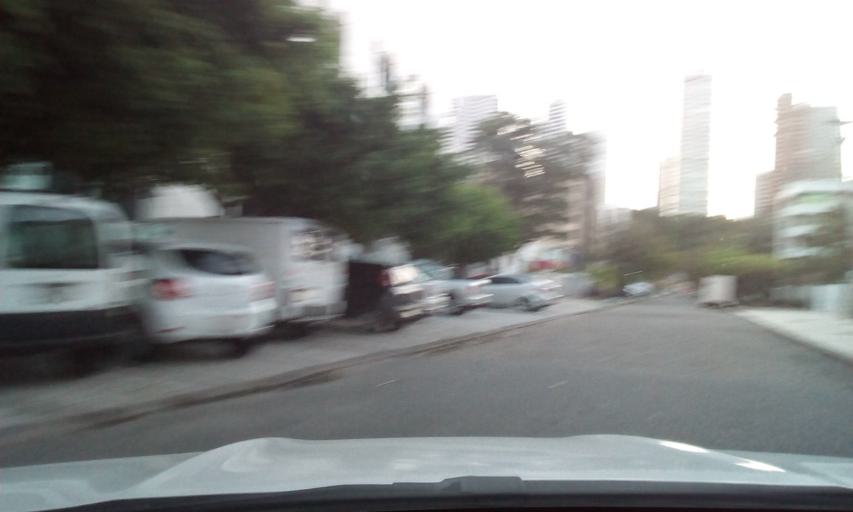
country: BR
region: Paraiba
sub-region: Joao Pessoa
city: Joao Pessoa
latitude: -7.1274
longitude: -34.8235
